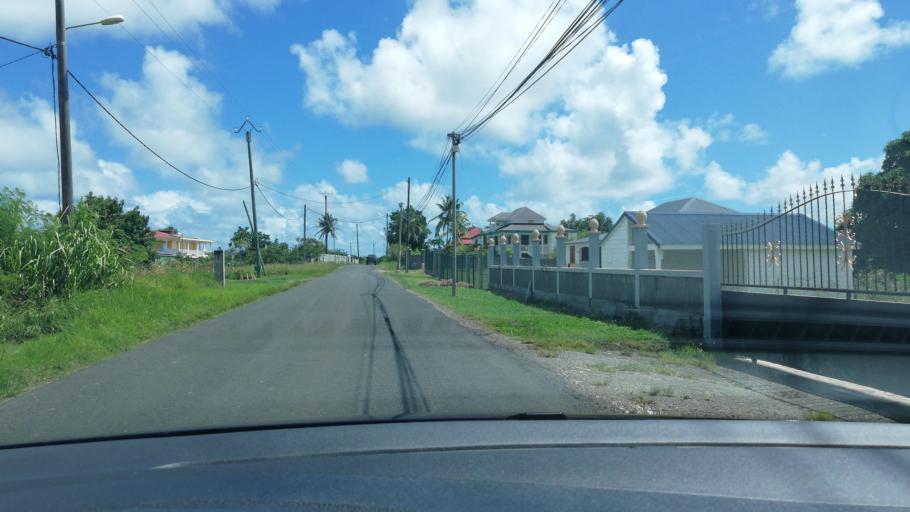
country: GP
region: Guadeloupe
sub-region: Guadeloupe
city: Petit-Canal
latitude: 16.3792
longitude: -61.4433
